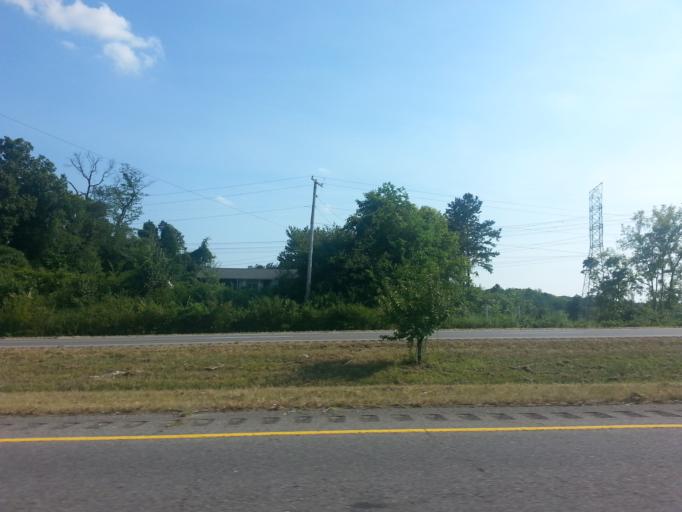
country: US
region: Tennessee
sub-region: Blount County
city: Maryville
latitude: 35.7534
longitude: -84.0087
